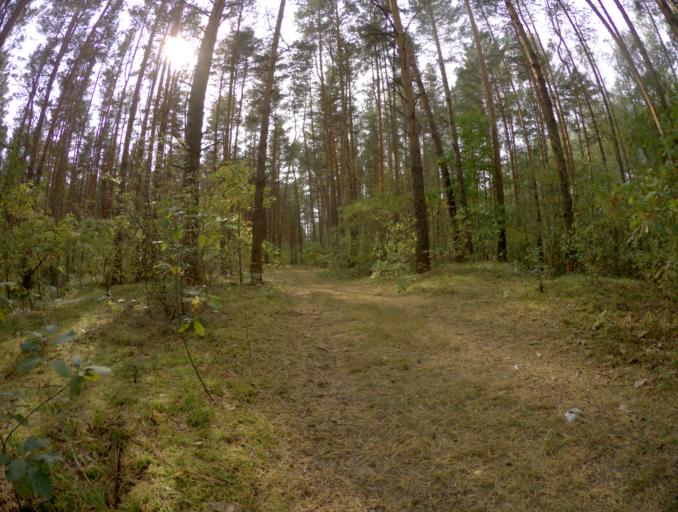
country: RU
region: Vladimir
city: Kommunar
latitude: 56.1343
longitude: 40.5003
